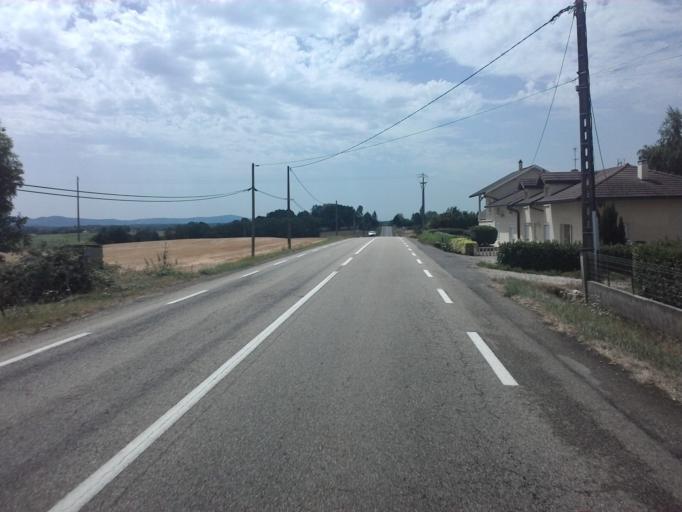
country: FR
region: Rhone-Alpes
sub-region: Departement de l'Ain
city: Coligny
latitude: 46.3428
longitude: 5.3198
